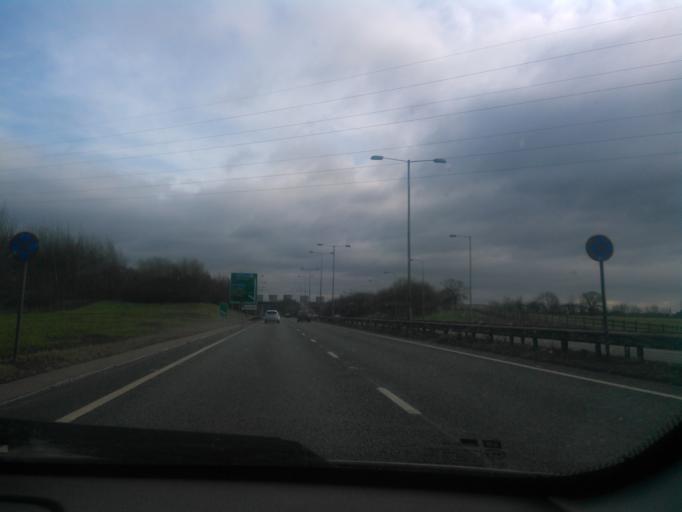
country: GB
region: England
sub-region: Derbyshire
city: Etwall
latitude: 52.8692
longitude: -1.5823
